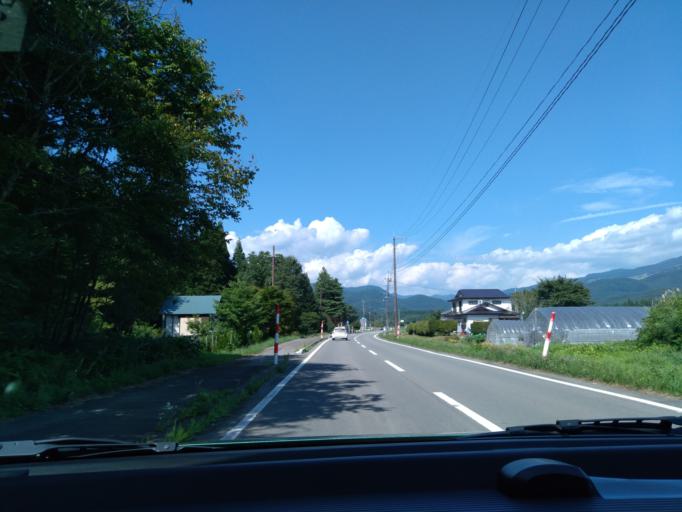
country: JP
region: Akita
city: Kakunodatemachi
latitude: 39.7361
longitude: 140.7082
